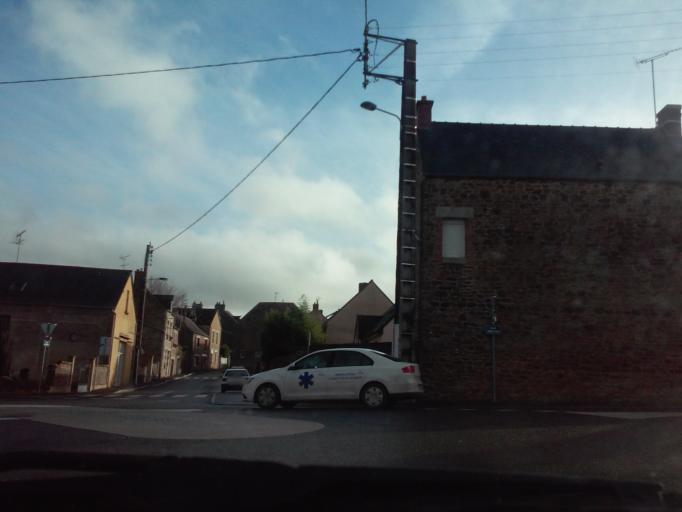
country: FR
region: Brittany
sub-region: Departement d'Ille-et-Vilaine
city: Fougeres
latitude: 48.3618
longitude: -1.1933
